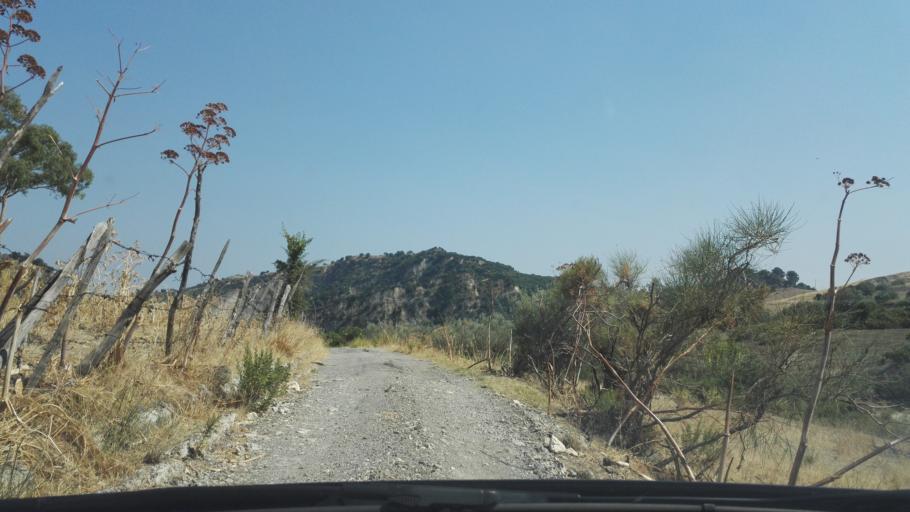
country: IT
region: Calabria
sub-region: Provincia di Reggio Calabria
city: Stilo
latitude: 38.4564
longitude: 16.4643
